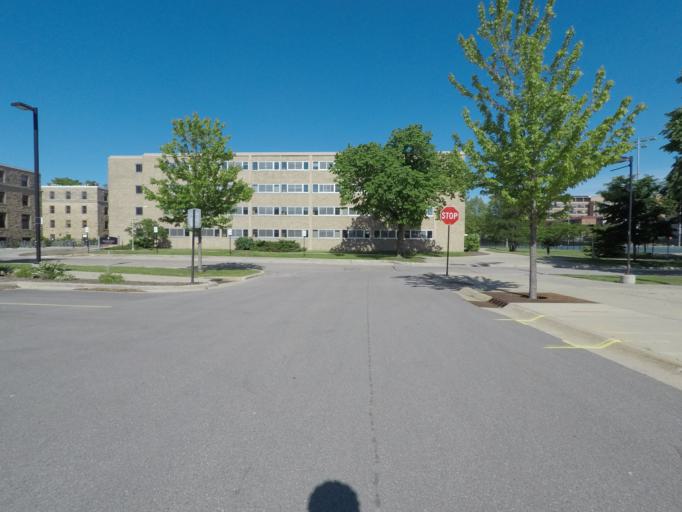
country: US
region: Wisconsin
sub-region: Dane County
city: Madison
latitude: 43.0775
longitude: -89.4162
